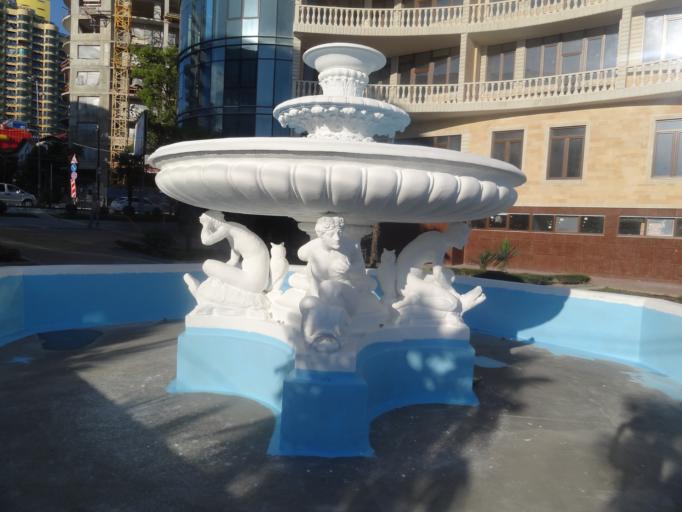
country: RU
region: Krasnodarskiy
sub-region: Sochi City
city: Sochi
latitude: 43.5666
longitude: 39.7376
